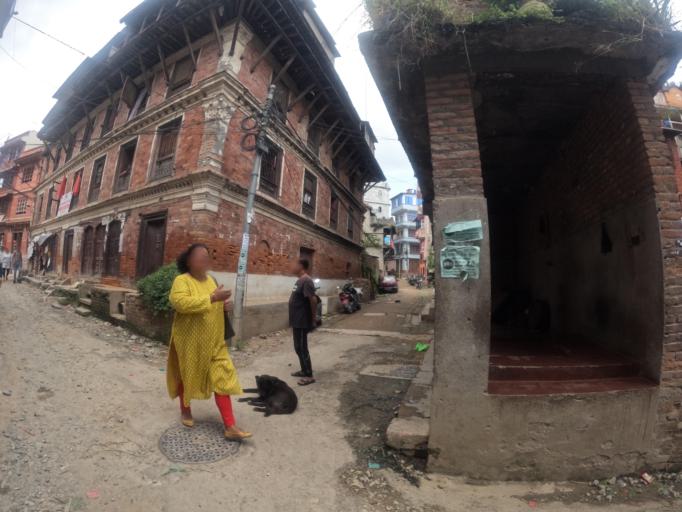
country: NP
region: Central Region
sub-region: Bagmati Zone
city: Bhaktapur
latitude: 27.6840
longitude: 85.3857
